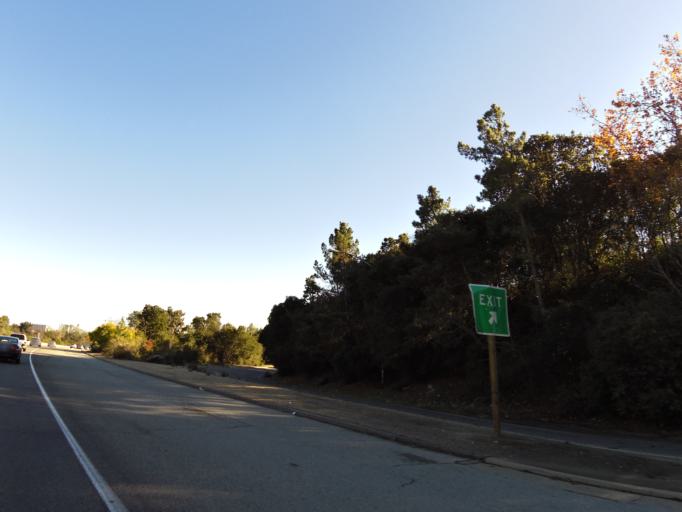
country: US
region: California
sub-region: Santa Clara County
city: Loyola
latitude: 37.3543
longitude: -122.1105
